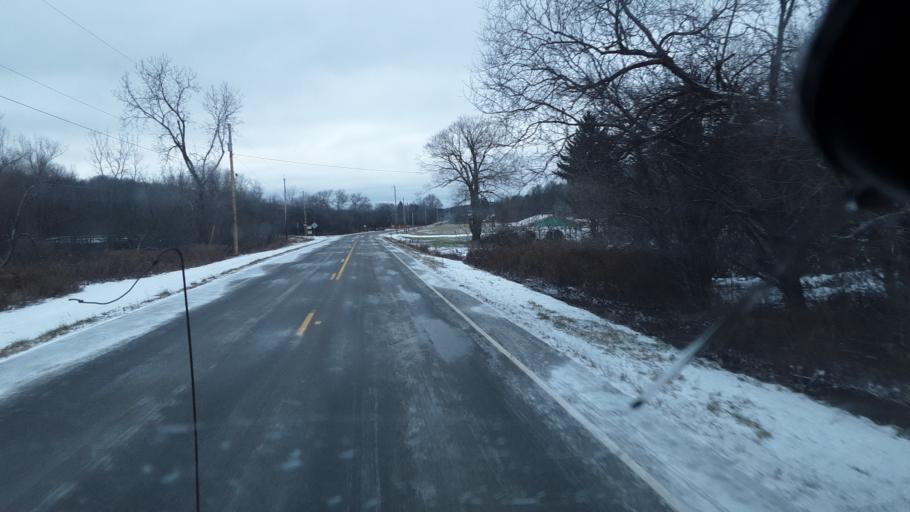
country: US
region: New York
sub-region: Allegany County
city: Friendship
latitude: 42.2772
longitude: -78.1304
